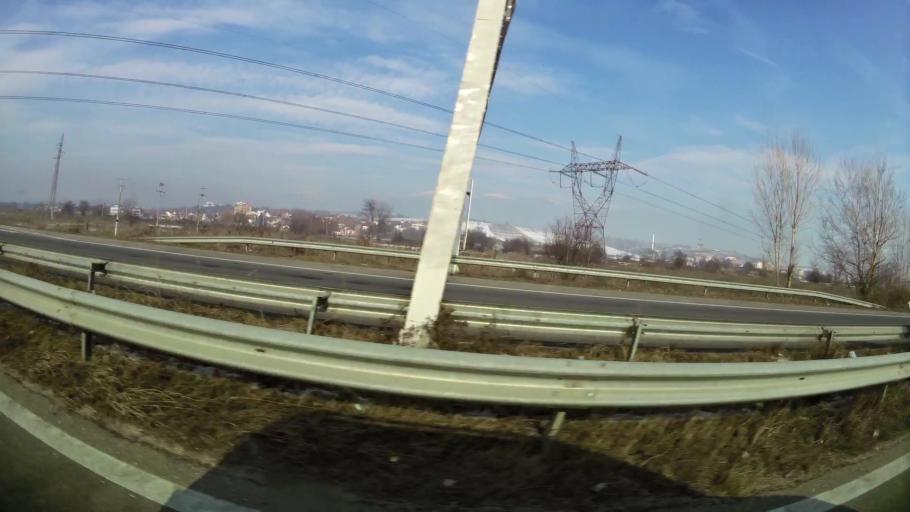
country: MK
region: Butel
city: Butel
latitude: 42.0399
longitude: 21.4601
